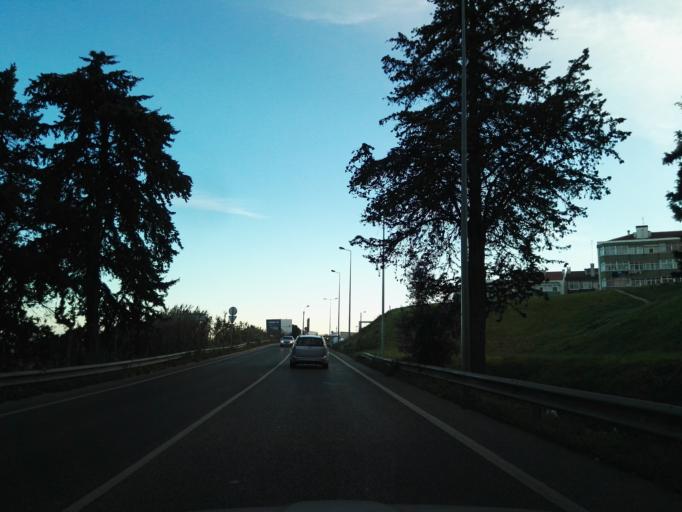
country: PT
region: Lisbon
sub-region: Vila Franca de Xira
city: Vialonga
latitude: 38.8757
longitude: -9.0527
